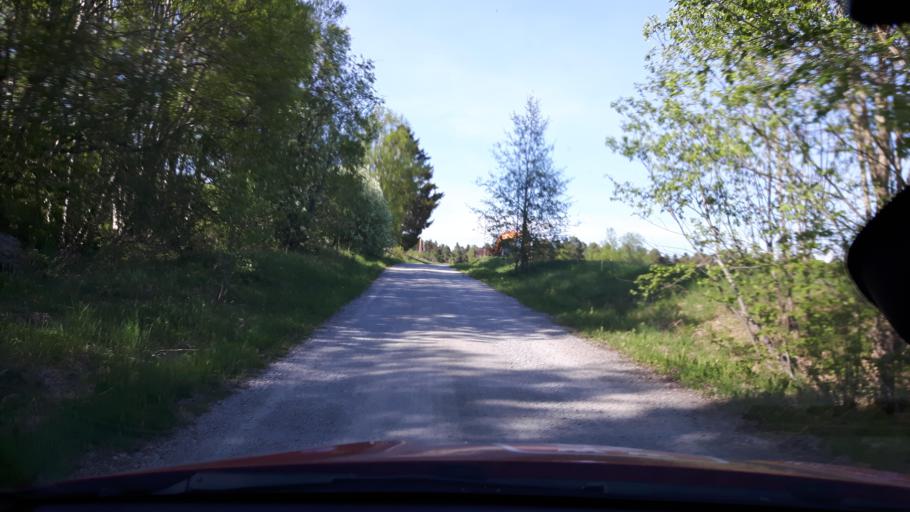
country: SE
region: Jaemtland
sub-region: Bergs Kommun
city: Hoverberg
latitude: 62.9152
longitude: 14.5215
